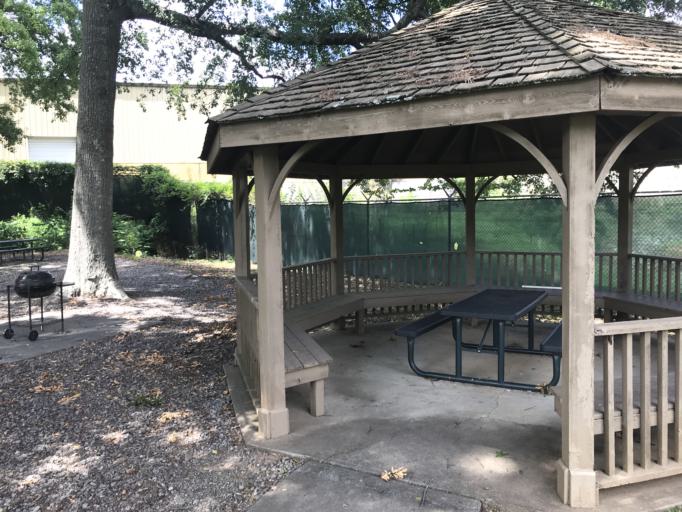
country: US
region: Georgia
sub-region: Cobb County
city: Marietta
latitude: 33.9378
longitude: -84.5406
